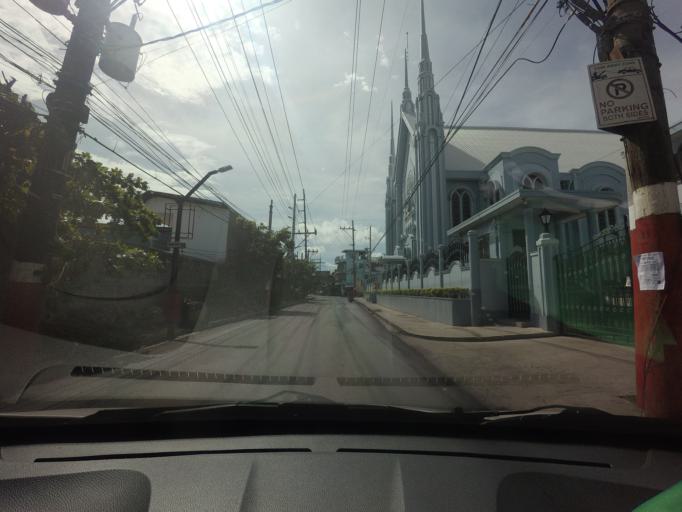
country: PH
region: Calabarzon
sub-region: Province of Rizal
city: Pateros
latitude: 14.5401
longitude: 121.0913
